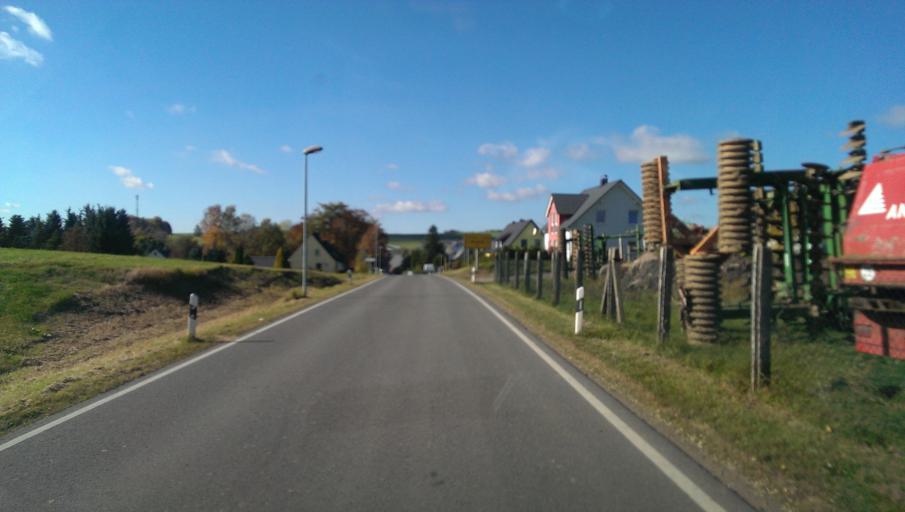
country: DE
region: Saxony
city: Grosshartmannsdorf
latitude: 50.8005
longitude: 13.3255
